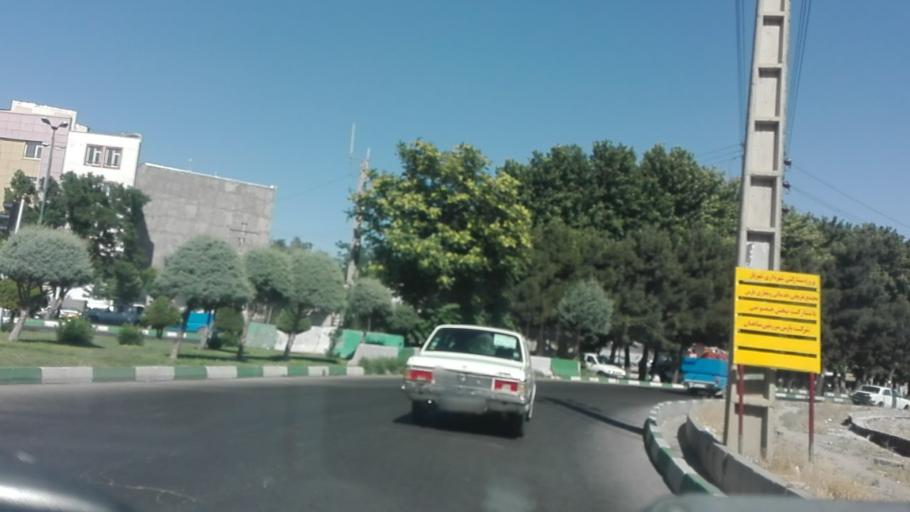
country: IR
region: Tehran
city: Shahriar
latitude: 35.6547
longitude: 51.0500
